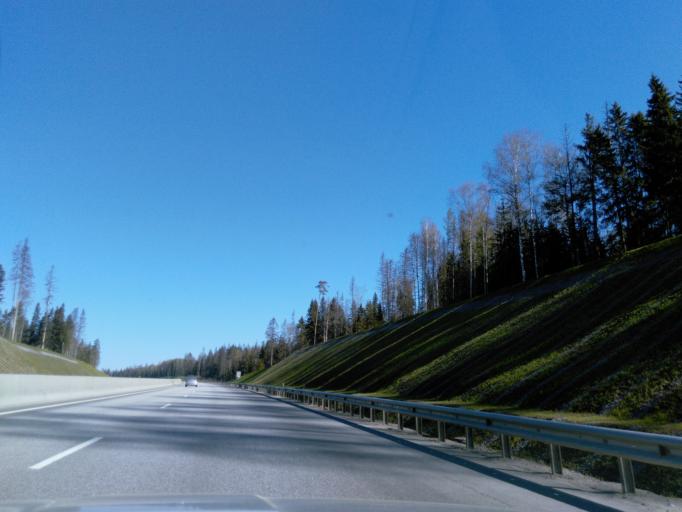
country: RU
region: Moskovskaya
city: Rzhavki
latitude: 56.0409
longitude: 37.2677
